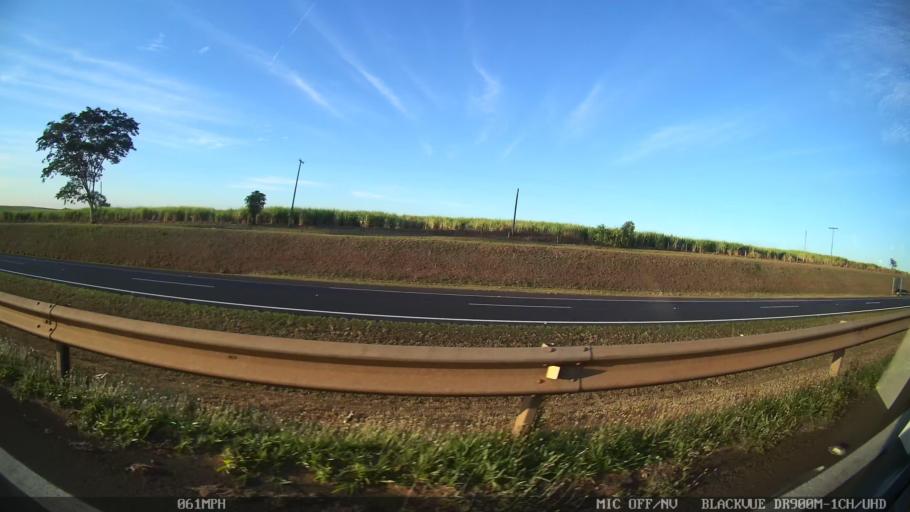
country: BR
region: Sao Paulo
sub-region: Catanduva
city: Catanduva
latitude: -21.0797
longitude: -49.0907
